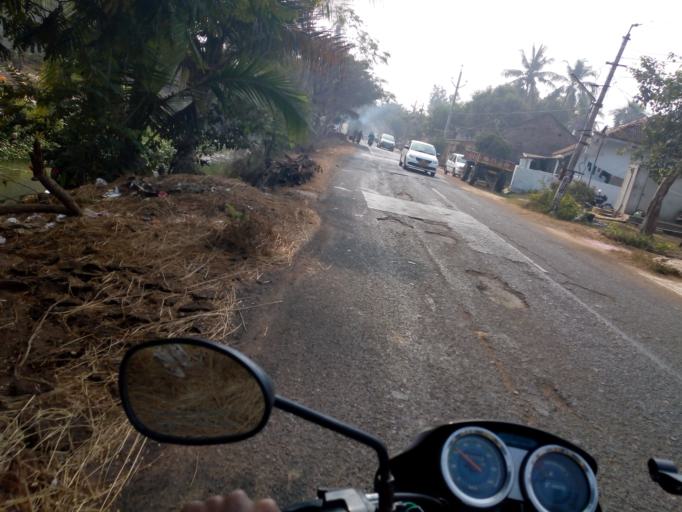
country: IN
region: Andhra Pradesh
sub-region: West Godavari
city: Tadepallegudem
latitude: 16.7805
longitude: 81.4204
